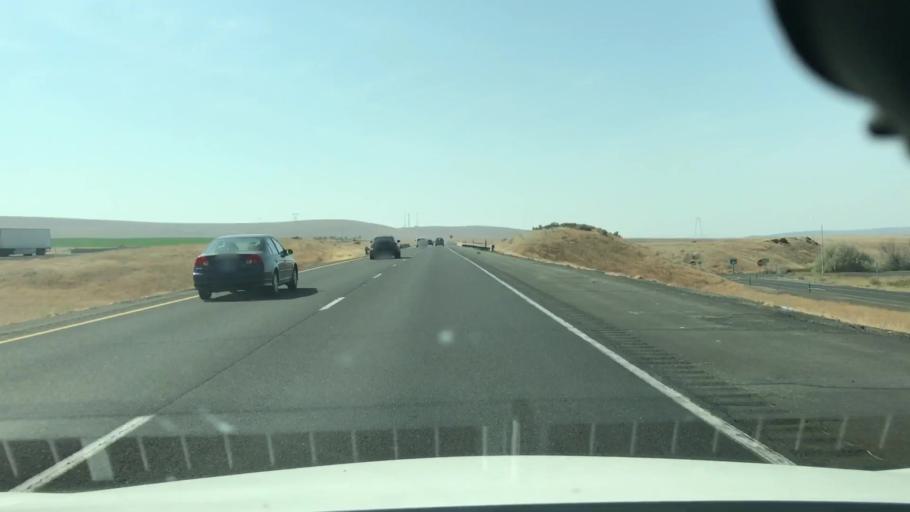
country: US
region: Washington
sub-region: Grant County
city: Quincy
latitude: 47.0228
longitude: -119.9438
